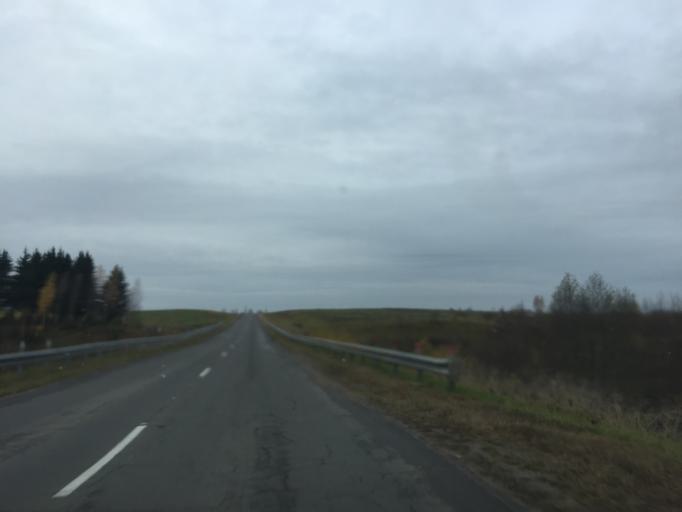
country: BY
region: Mogilev
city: Horki
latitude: 54.3121
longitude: 30.9510
